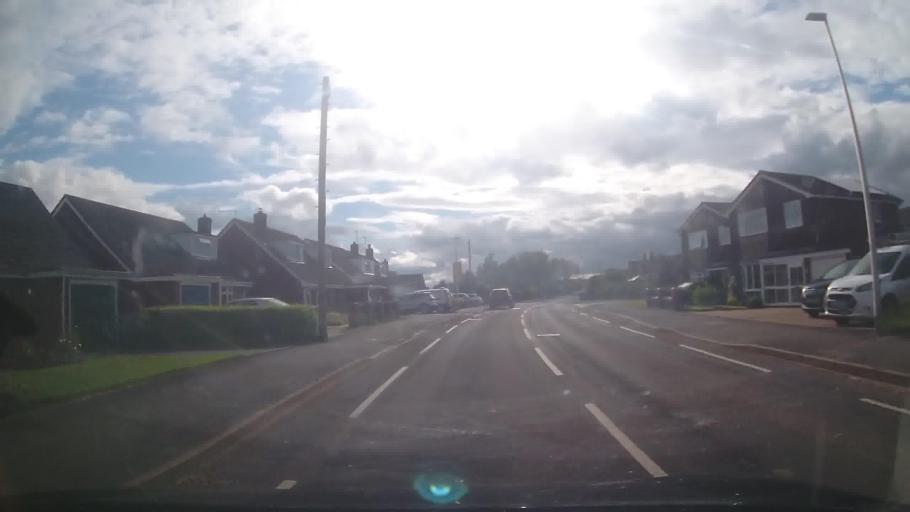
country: GB
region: England
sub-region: Shropshire
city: Wem
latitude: 52.8597
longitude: -2.7244
